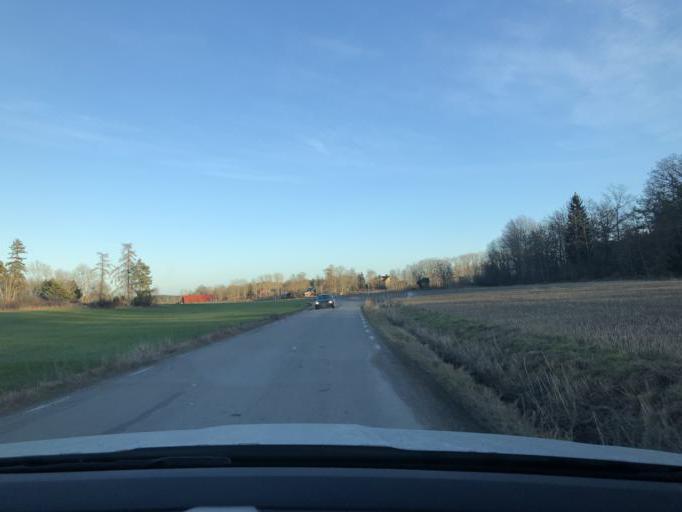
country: SE
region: Soedermanland
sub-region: Eskilstuna Kommun
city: Arla
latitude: 59.4159
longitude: 16.6822
